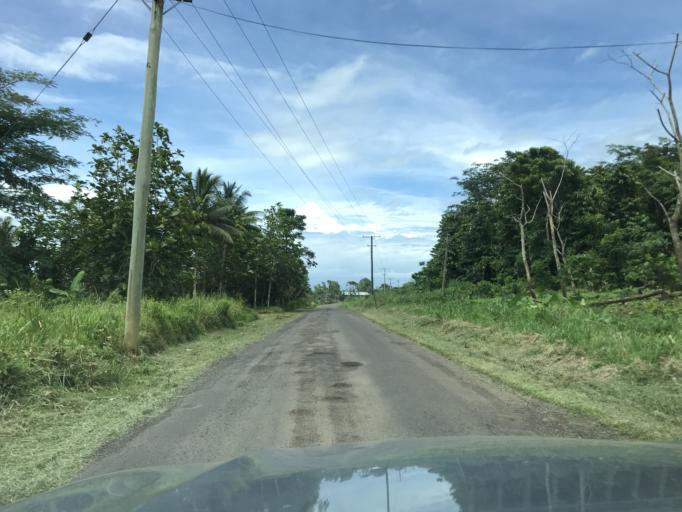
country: WS
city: Fasito`outa
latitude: -13.8615
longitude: -171.9101
